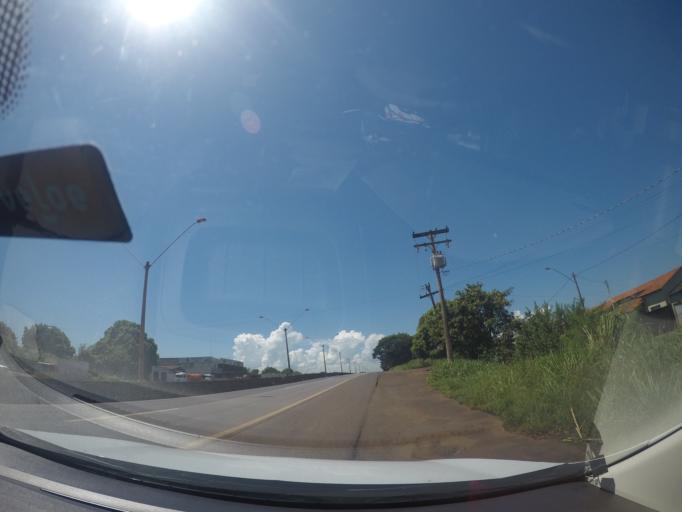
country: BR
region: Goias
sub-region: Itumbiara
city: Itumbiara
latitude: -18.4083
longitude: -49.1975
